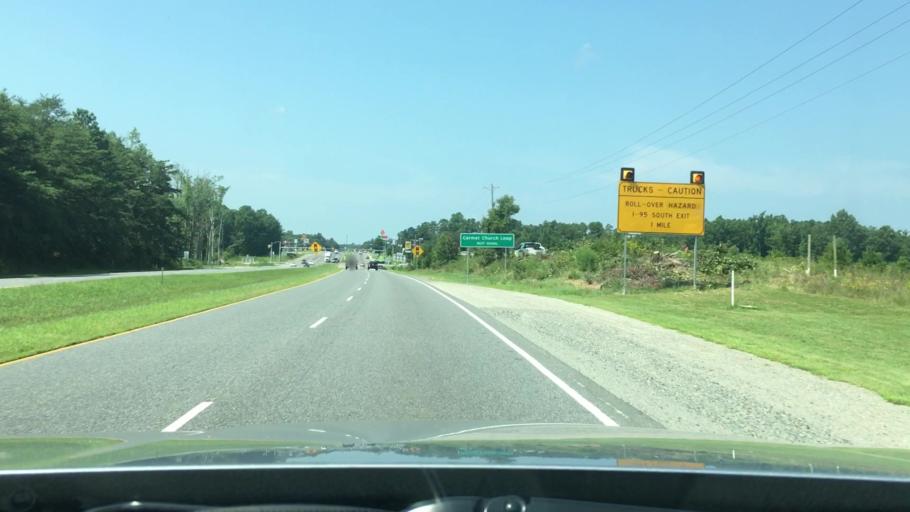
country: US
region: Virginia
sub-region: Caroline County
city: Bowling Green
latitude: 37.9428
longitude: -77.4584
